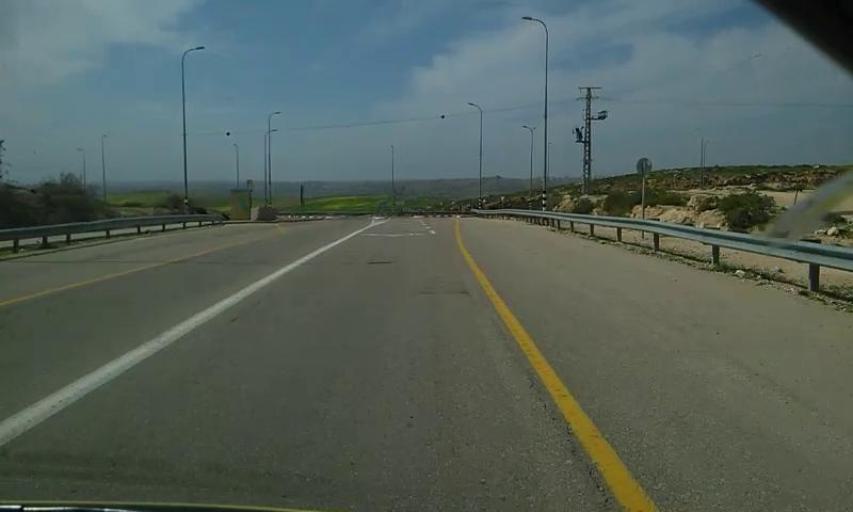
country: PS
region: West Bank
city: Az Zahiriyah
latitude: 31.3769
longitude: 35.0044
